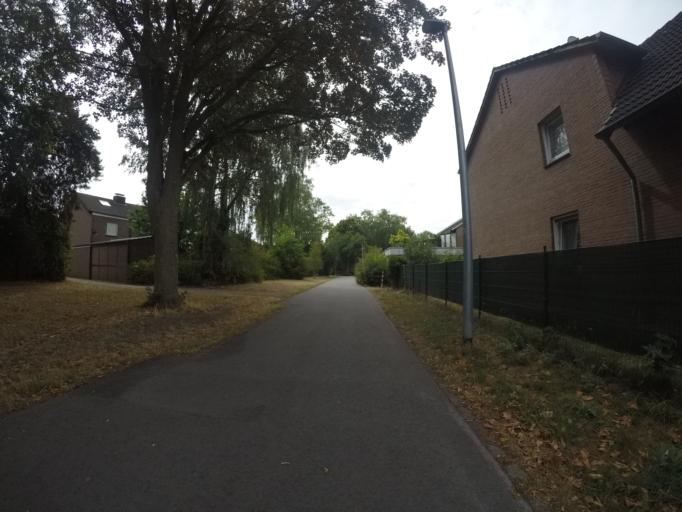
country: DE
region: North Rhine-Westphalia
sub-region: Regierungsbezirk Dusseldorf
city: Bocholt
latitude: 51.8456
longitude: 6.5943
